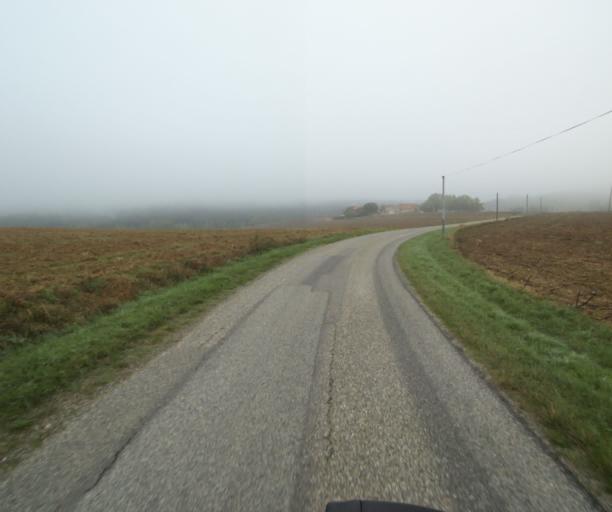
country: FR
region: Midi-Pyrenees
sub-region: Departement du Tarn-et-Garonne
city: Nohic
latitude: 43.9267
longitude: 1.4798
